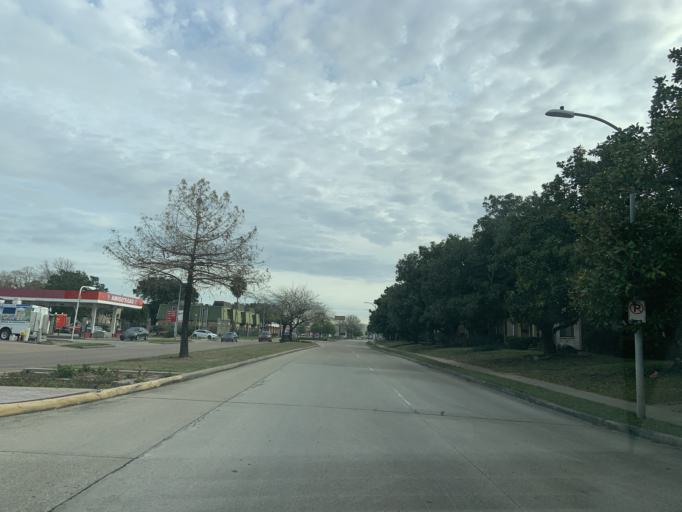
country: US
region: Texas
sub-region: Harris County
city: Bellaire
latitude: 29.6904
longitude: -95.5095
